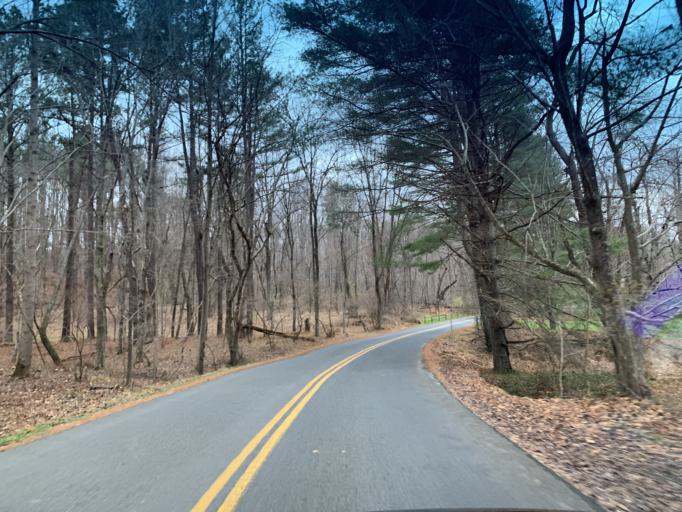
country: US
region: Maryland
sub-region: Harford County
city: Jarrettsville
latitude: 39.6371
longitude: -76.4249
